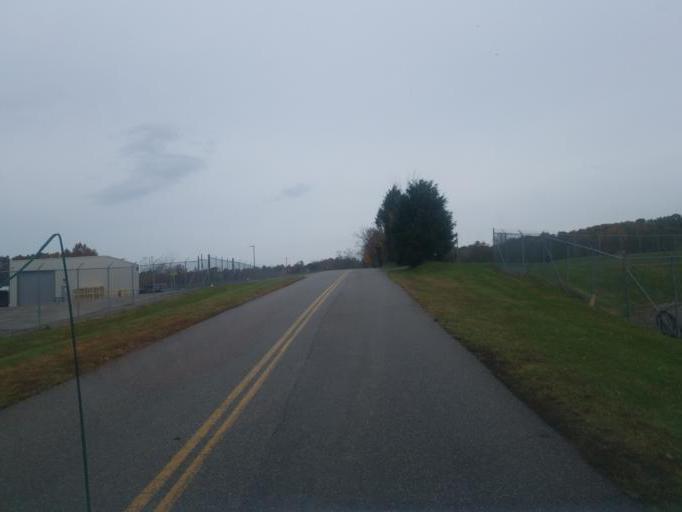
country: US
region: Ohio
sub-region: Washington County
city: Beverly
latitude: 39.5344
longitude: -81.7159
